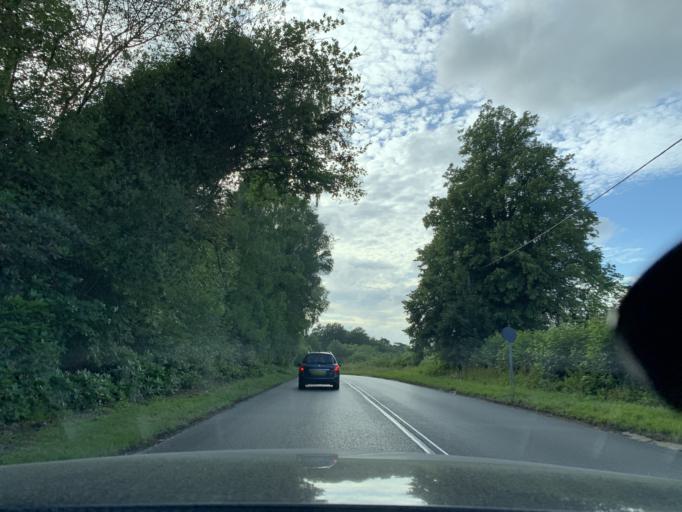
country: GB
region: England
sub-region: East Sussex
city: Robertsbridge
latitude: 50.9578
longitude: 0.4945
